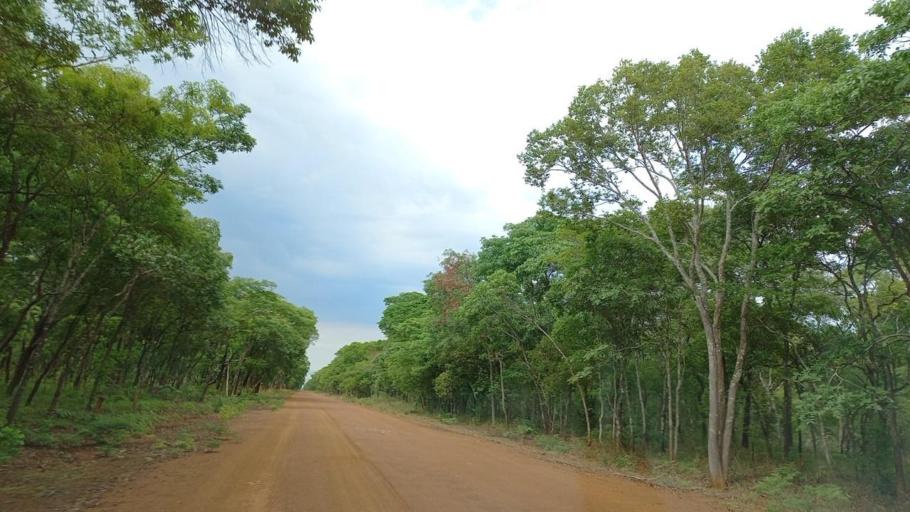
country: ZM
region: North-Western
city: Kalengwa
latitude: -13.4185
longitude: 25.0568
